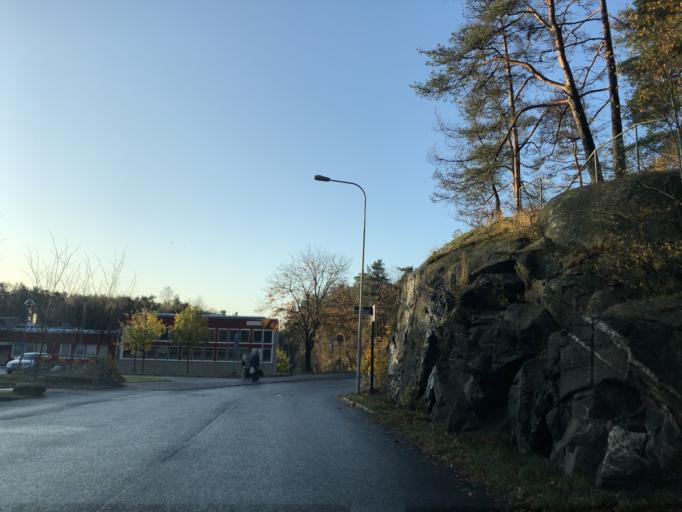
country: SE
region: Vaestra Goetaland
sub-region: Goteborg
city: Hammarkullen
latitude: 57.7787
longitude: 12.0301
